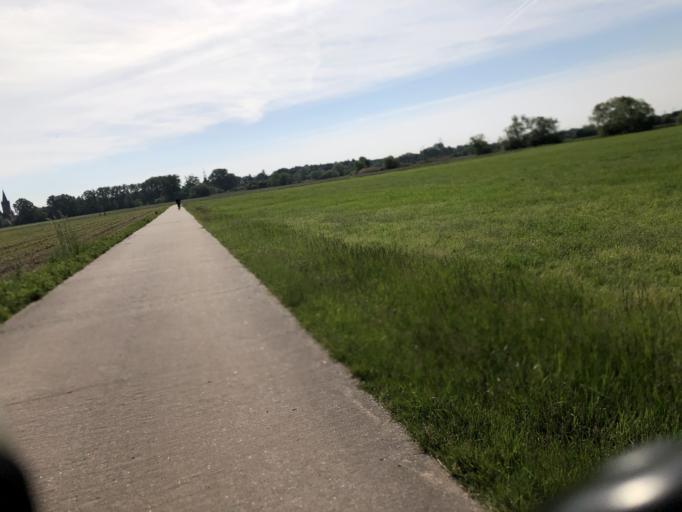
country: DE
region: Bavaria
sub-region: Regierungsbezirk Mittelfranken
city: Erlangen
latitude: 49.5721
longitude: 10.9725
